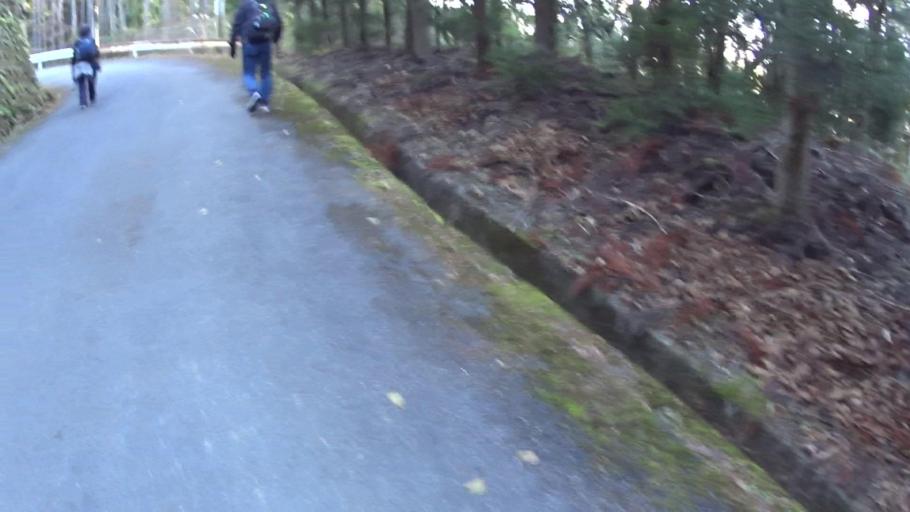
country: JP
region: Kyoto
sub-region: Kyoto-shi
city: Kamigyo-ku
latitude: 35.0768
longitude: 135.7207
